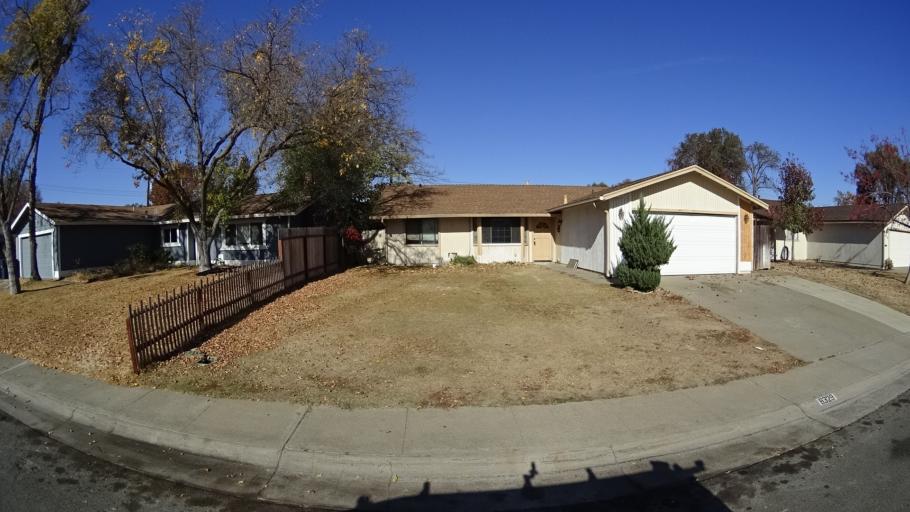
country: US
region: California
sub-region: Sacramento County
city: Antelope
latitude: 38.6850
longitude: -121.3166
